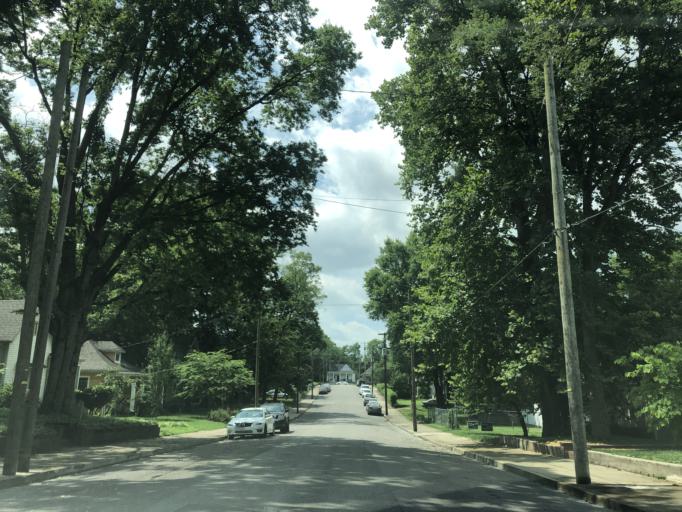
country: US
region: Tennessee
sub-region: Davidson County
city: Nashville
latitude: 36.1899
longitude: -86.7652
